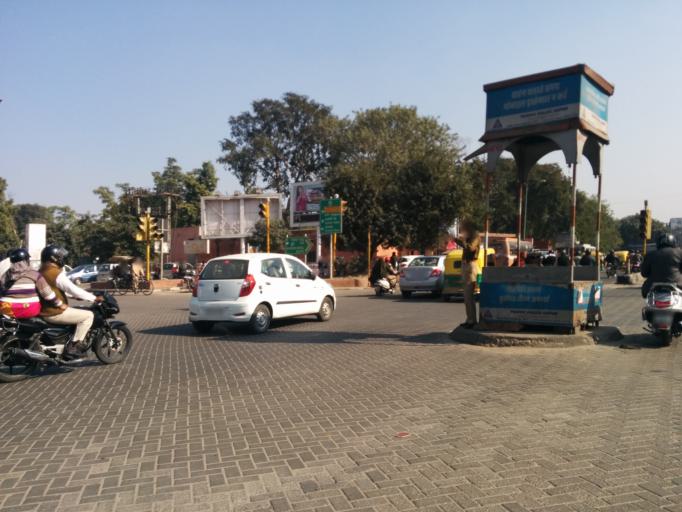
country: IN
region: Rajasthan
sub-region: Jaipur
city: Jaipur
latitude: 26.9179
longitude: 75.8012
